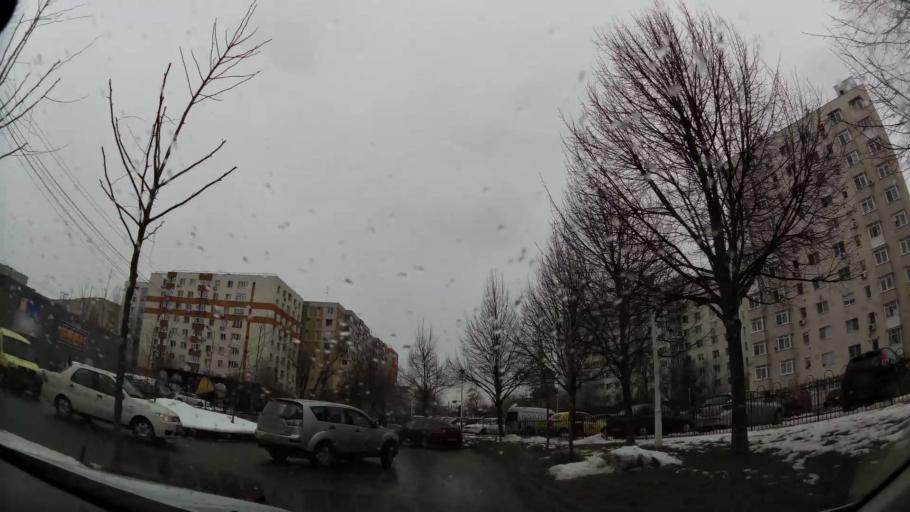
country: RO
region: Ilfov
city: Dobroesti
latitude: 44.4232
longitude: 26.1797
